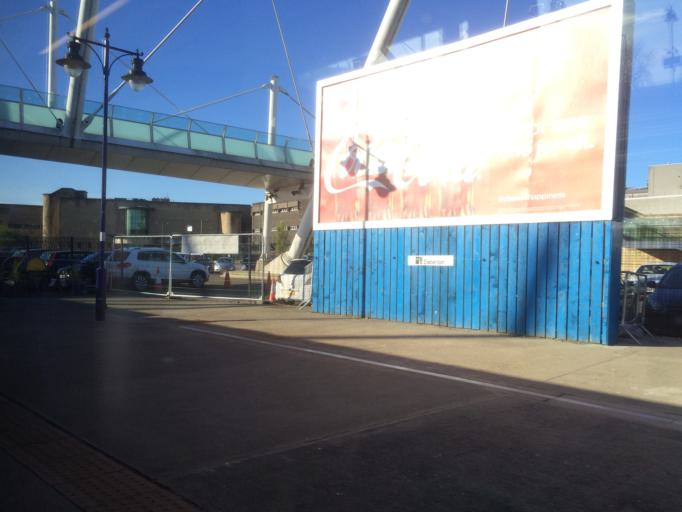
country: GB
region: Scotland
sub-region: Stirling
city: Stirling
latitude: 56.1195
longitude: -3.9345
